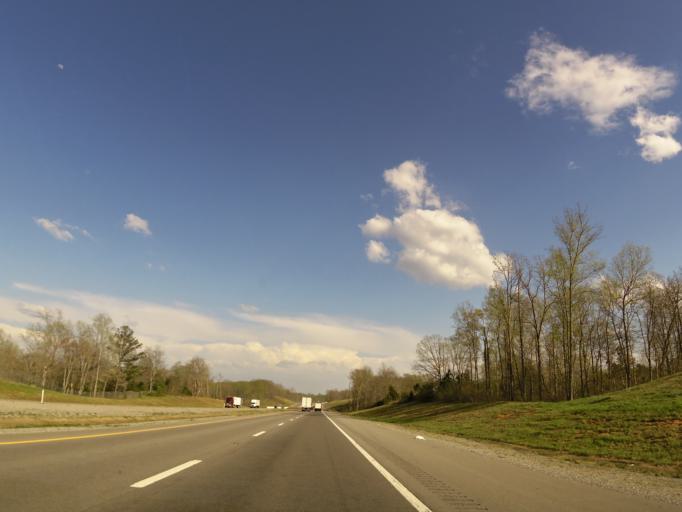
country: US
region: Tennessee
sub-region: Williamson County
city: Fairview
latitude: 35.8622
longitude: -87.0861
